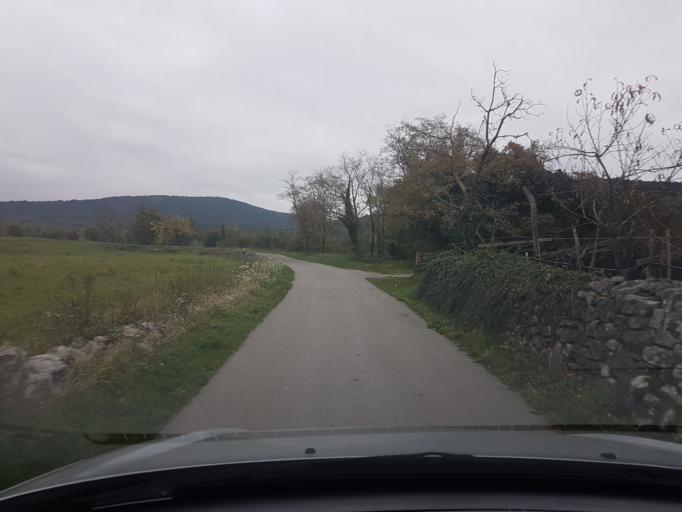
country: SI
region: Sezana
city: Sezana
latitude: 45.7372
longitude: 13.9309
